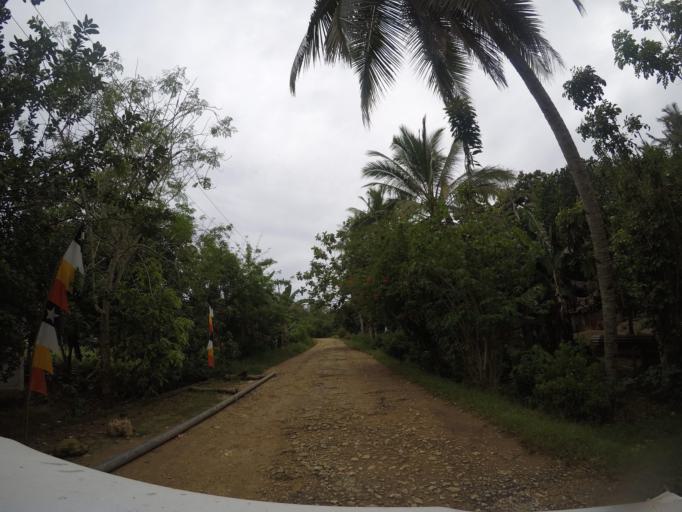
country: TL
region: Lautem
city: Lospalos
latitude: -8.5349
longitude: 126.9968
